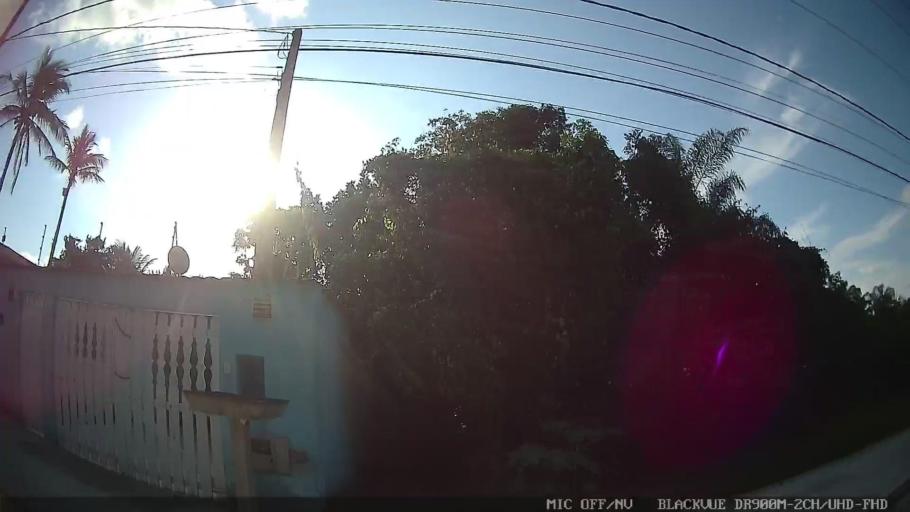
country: BR
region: Sao Paulo
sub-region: Itanhaem
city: Itanhaem
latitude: -24.1751
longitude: -46.8209
